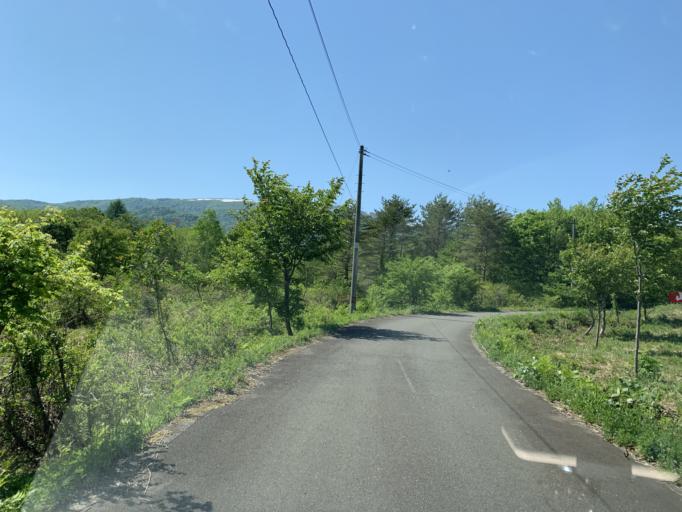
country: JP
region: Iwate
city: Shizukuishi
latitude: 39.5475
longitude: 140.8210
